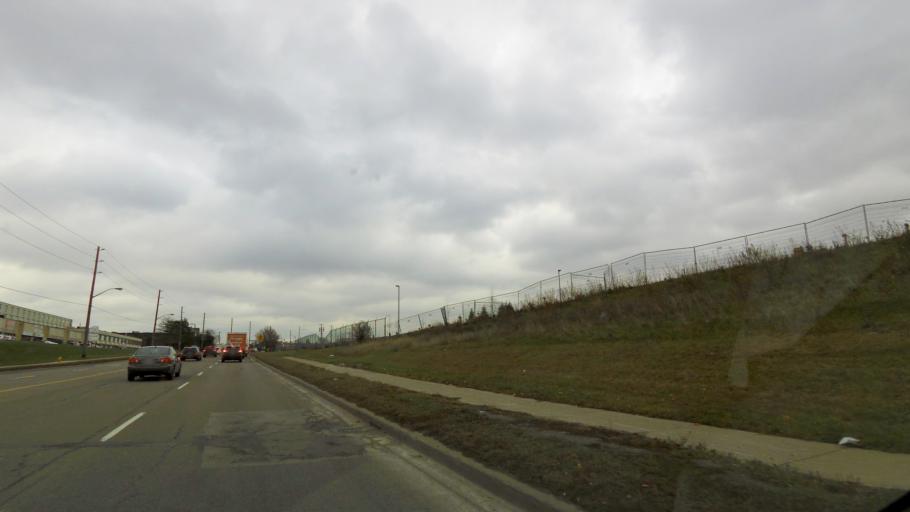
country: CA
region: Ontario
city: Concord
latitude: 43.7549
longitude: -79.4776
